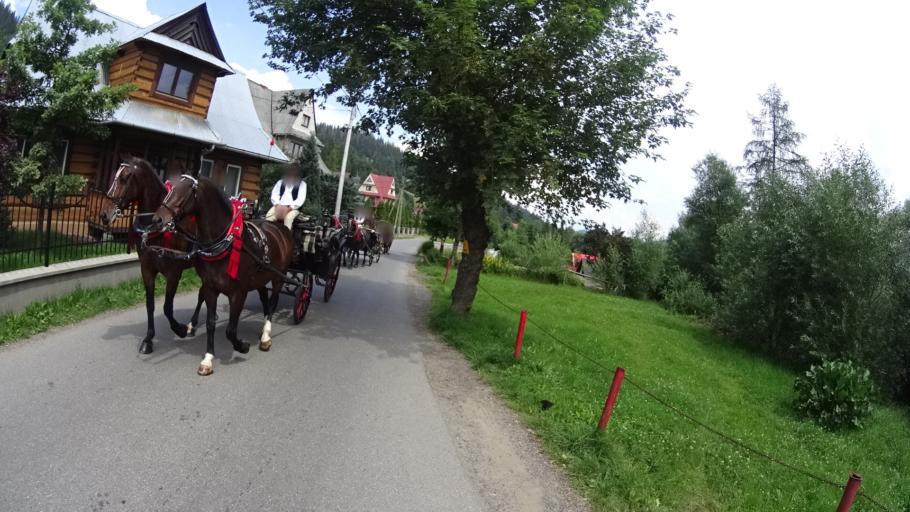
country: PL
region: Lesser Poland Voivodeship
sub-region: Powiat tatrzanski
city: Poronin
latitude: 49.3221
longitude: 19.9842
